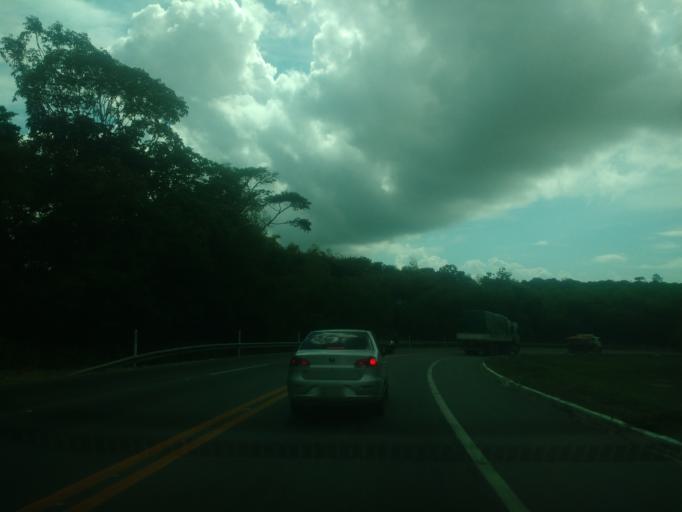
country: BR
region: Alagoas
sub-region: Marechal Deodoro
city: Marechal Deodoro
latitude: -9.6856
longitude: -35.8213
